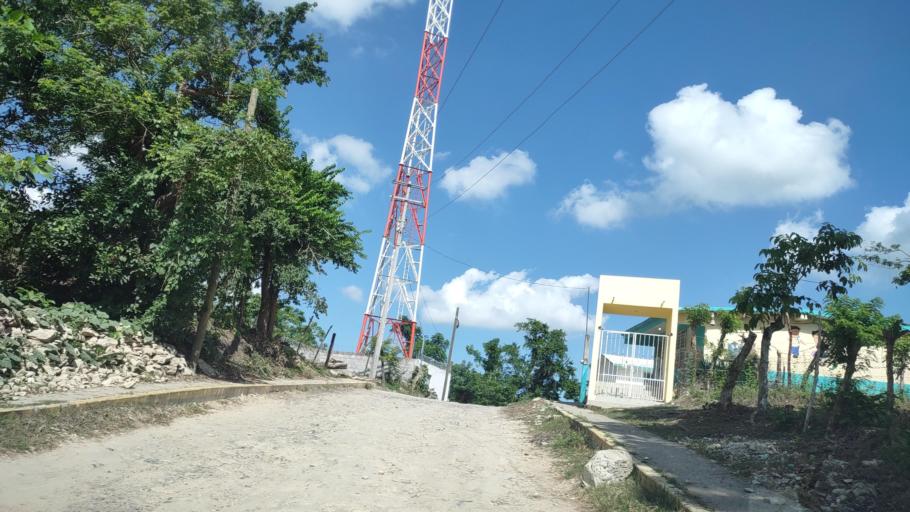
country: MM
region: Shan
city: Taunggyi
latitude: 20.5875
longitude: 97.3727
